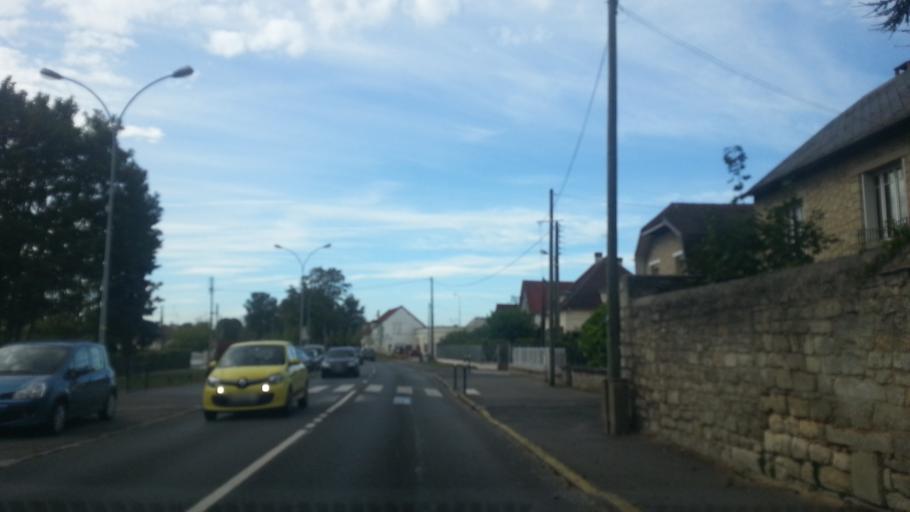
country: FR
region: Picardie
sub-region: Departement de l'Oise
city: Senlis
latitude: 49.2073
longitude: 2.5763
